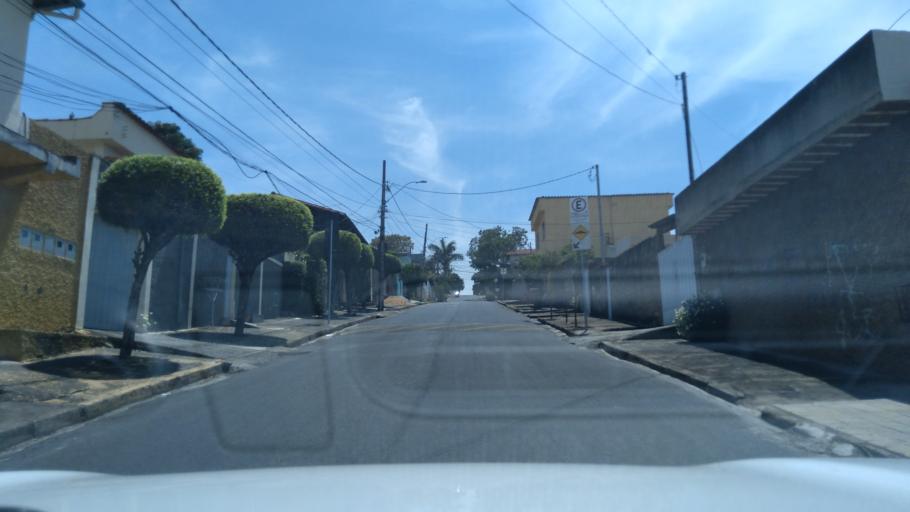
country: BR
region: Minas Gerais
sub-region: Contagem
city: Contagem
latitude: -19.9026
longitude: -44.0171
